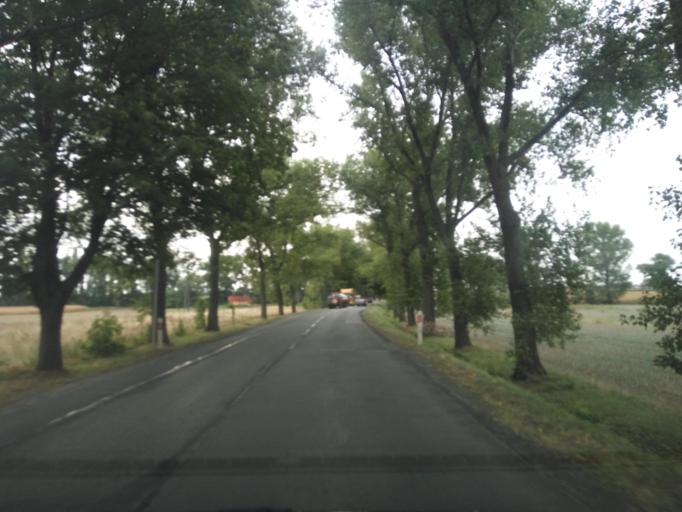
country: PL
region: Lower Silesian Voivodeship
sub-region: Powiat strzelinski
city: Strzelin
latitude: 50.8084
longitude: 17.0605
